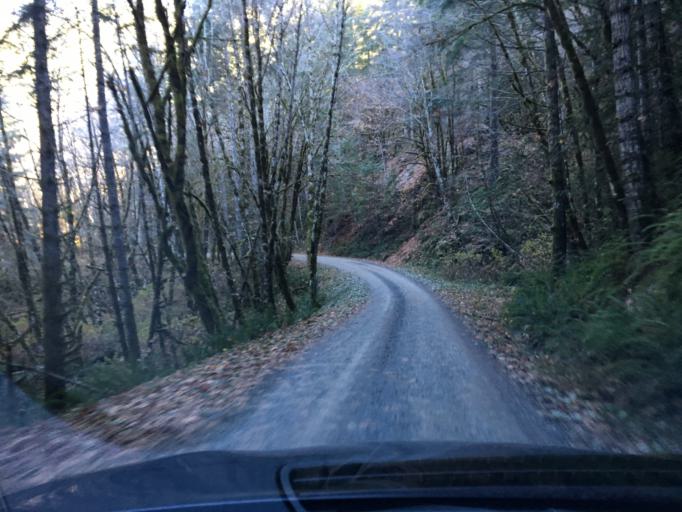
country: US
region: Oregon
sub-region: Douglas County
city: Winston
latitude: 43.3205
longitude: -123.5792
